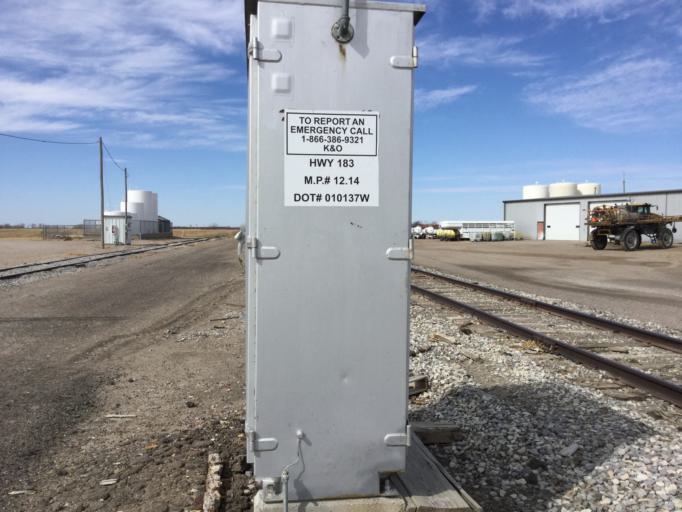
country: US
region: Kansas
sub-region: Pawnee County
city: Larned
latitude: 38.1810
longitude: -99.3145
